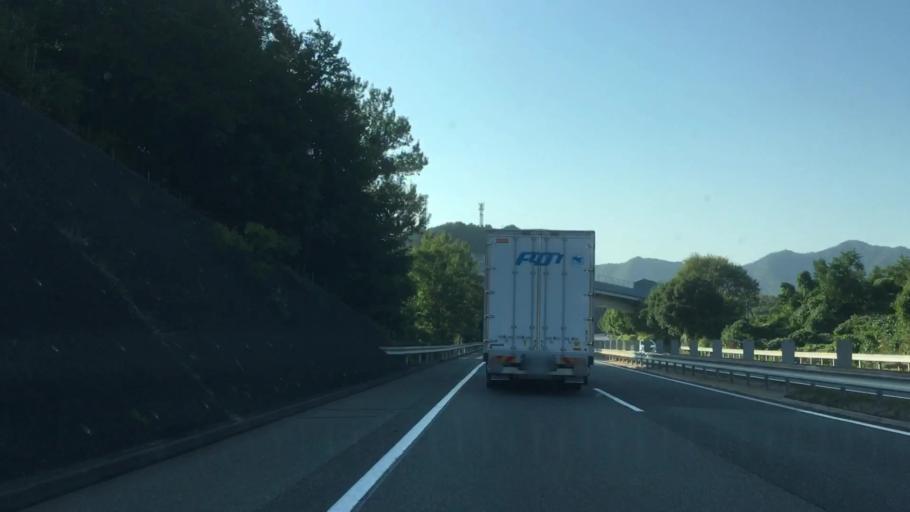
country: JP
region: Yamaguchi
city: Ogori-shimogo
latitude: 34.0873
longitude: 131.4642
